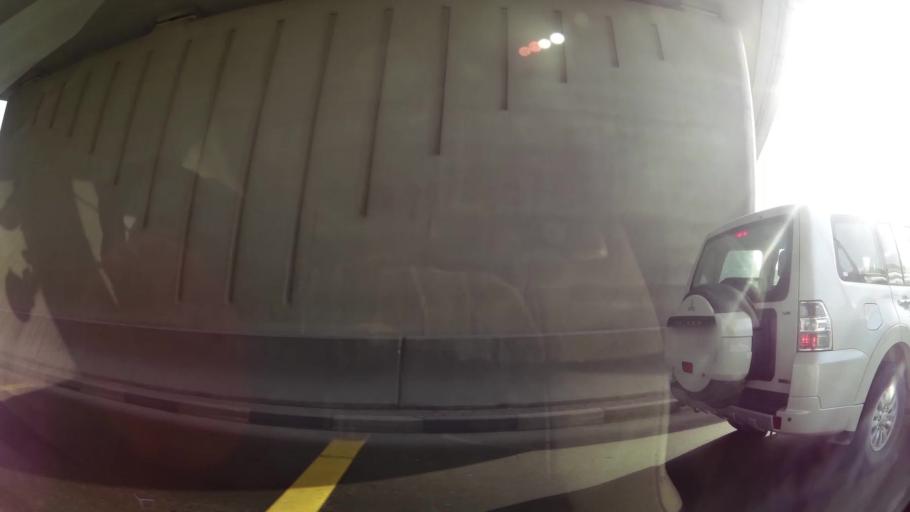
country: AE
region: Ash Shariqah
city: Sharjah
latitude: 25.2397
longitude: 55.3419
